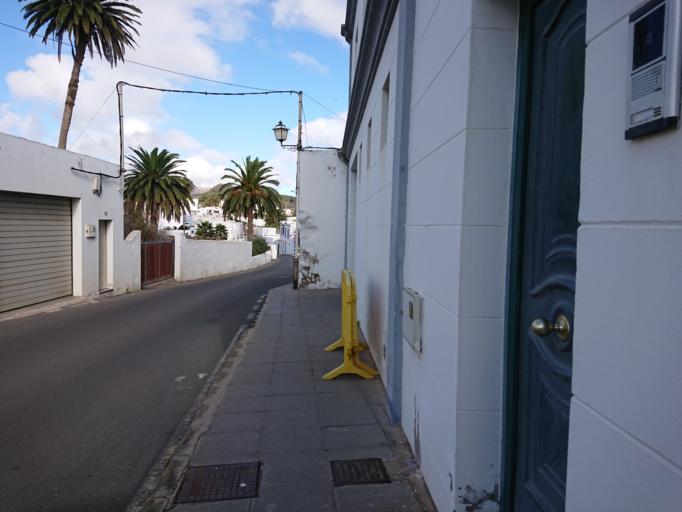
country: ES
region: Canary Islands
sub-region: Provincia de Las Palmas
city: Haria
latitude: 29.1447
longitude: -13.5020
